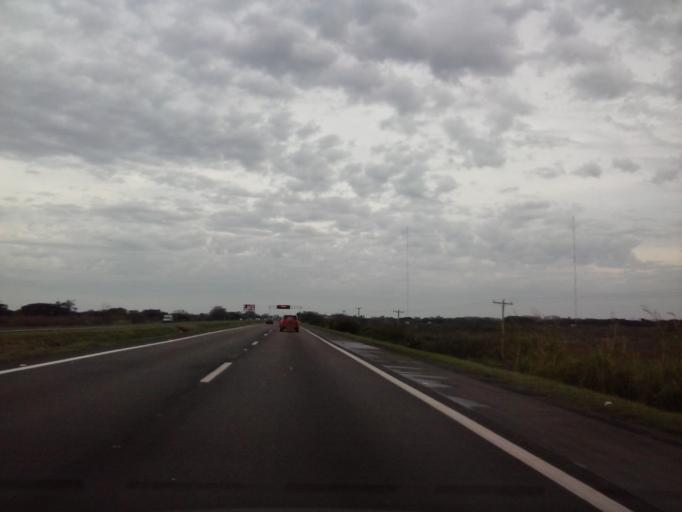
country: BR
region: Rio Grande do Sul
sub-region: Porto Alegre
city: Porto Alegre
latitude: -29.9989
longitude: -51.2942
